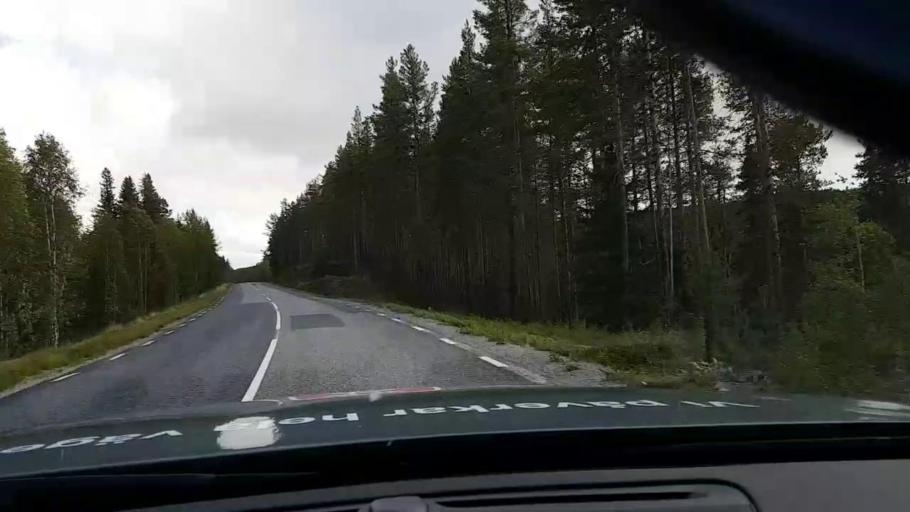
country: SE
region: Vaesterbotten
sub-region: Asele Kommun
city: Asele
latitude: 63.8427
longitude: 17.4243
